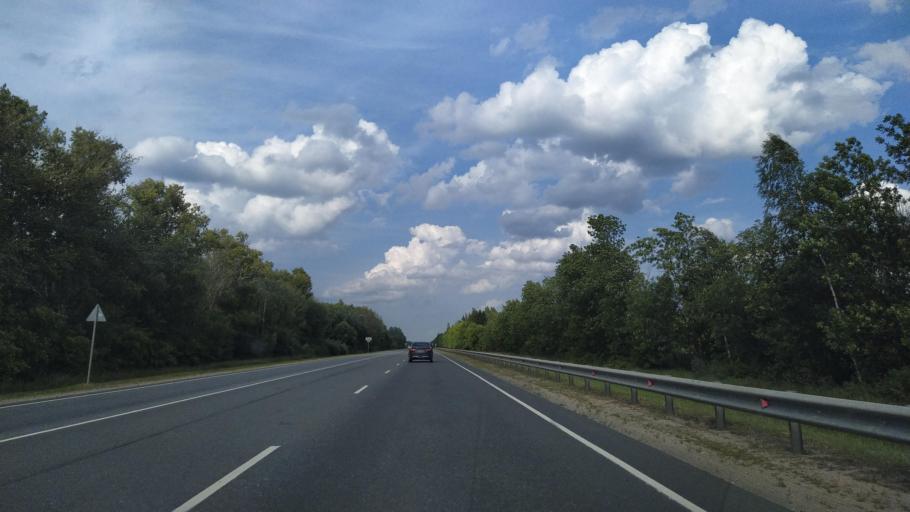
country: RU
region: Novgorod
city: Shimsk
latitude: 58.2313
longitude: 30.7577
